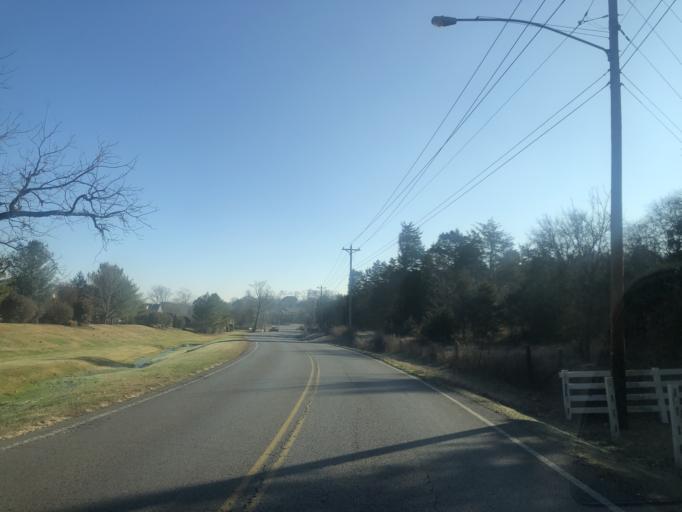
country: US
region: Tennessee
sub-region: Williamson County
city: Nolensville
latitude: 35.9691
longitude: -86.7172
